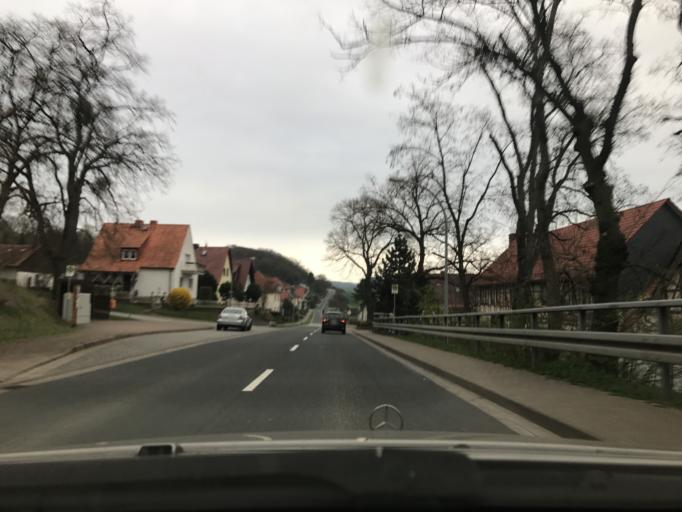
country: DE
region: Thuringia
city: Geisleden
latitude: 51.3505
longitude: 10.1984
